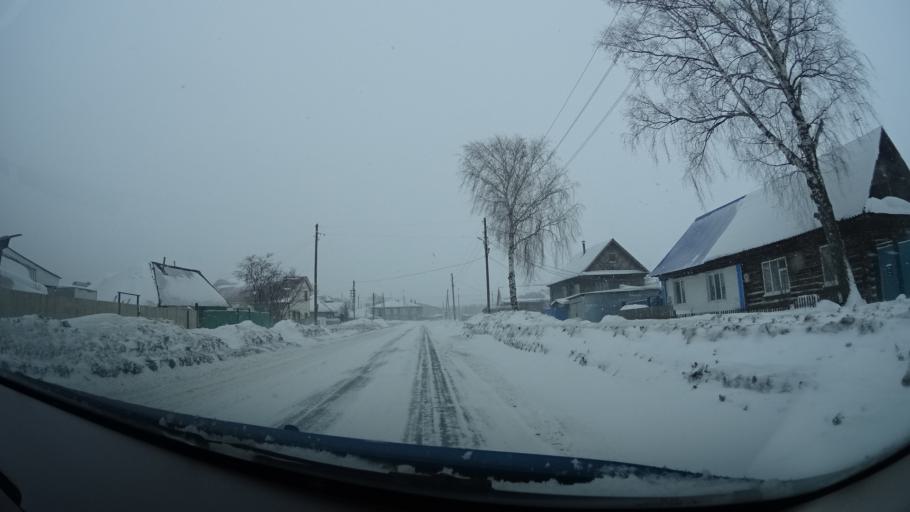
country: RU
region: Perm
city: Kuyeda
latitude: 56.4285
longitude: 55.5794
